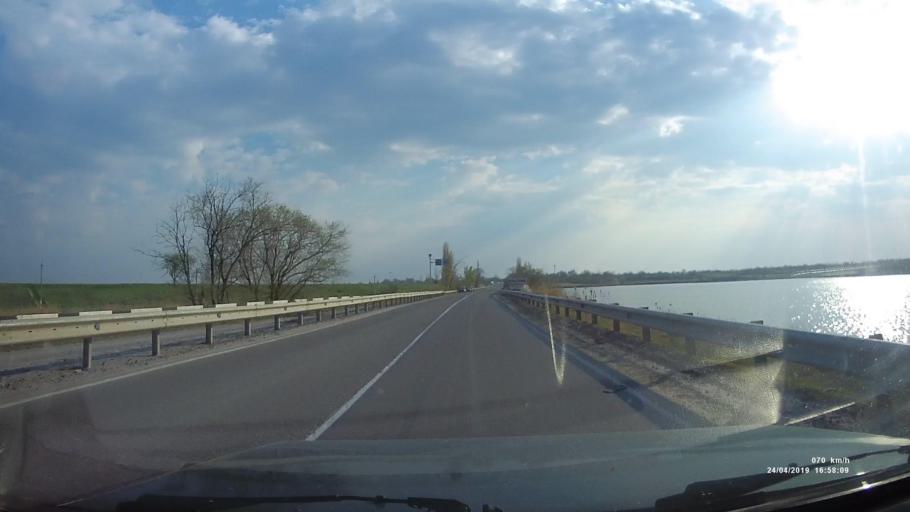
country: RU
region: Rostov
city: Proletarsk
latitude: 46.6300
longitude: 41.6627
